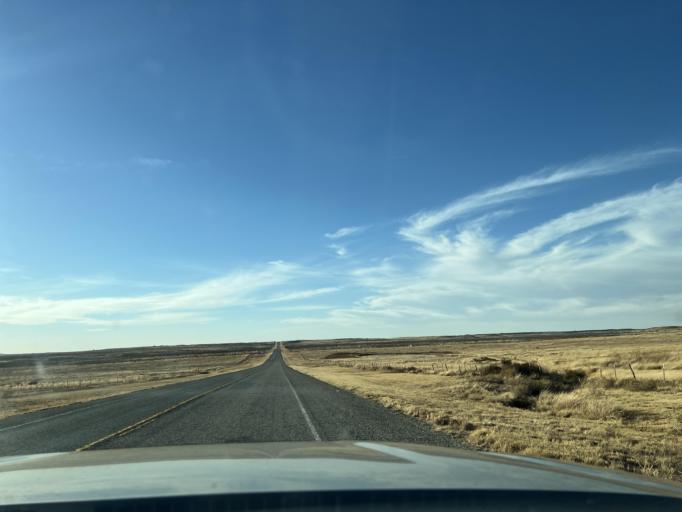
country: US
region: Texas
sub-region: Borden County
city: Gail
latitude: 32.7531
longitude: -101.2311
